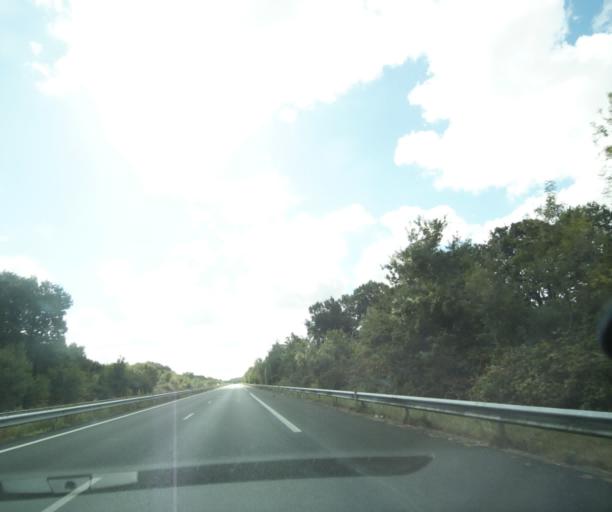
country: FR
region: Poitou-Charentes
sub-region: Departement de la Charente-Maritime
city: Cabariot
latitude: 45.9321
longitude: -0.8384
